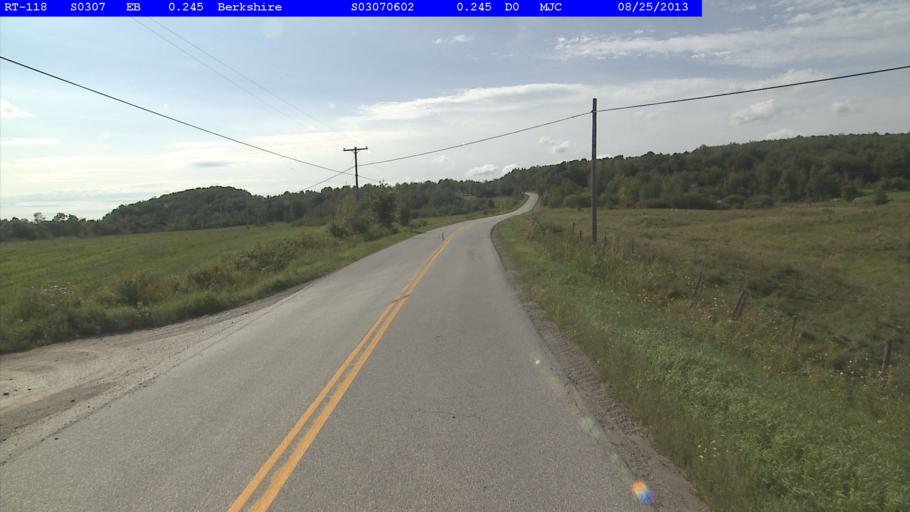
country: US
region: Vermont
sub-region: Franklin County
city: Richford
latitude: 44.9342
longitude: -72.7164
